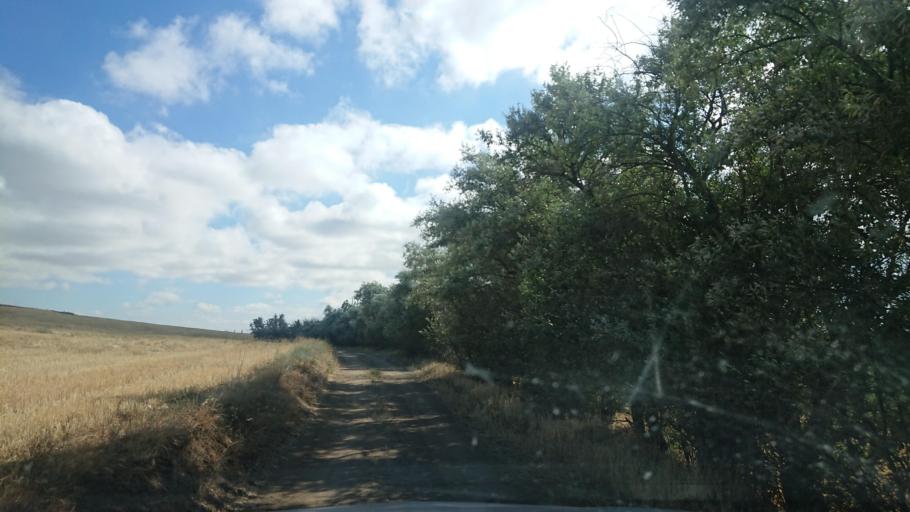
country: TR
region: Aksaray
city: Agacoren
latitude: 38.8555
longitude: 33.9333
